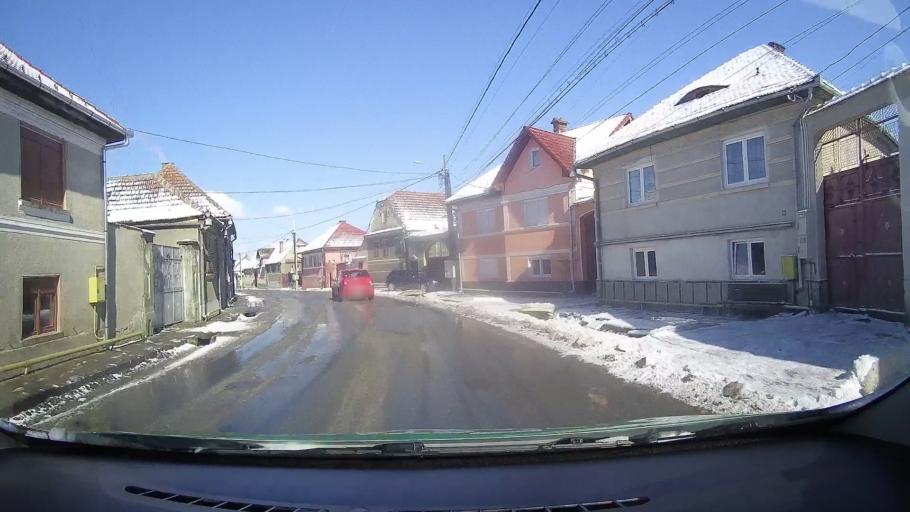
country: RO
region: Sibiu
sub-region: Comuna Racovita
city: Racovita
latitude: 45.6819
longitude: 24.3467
